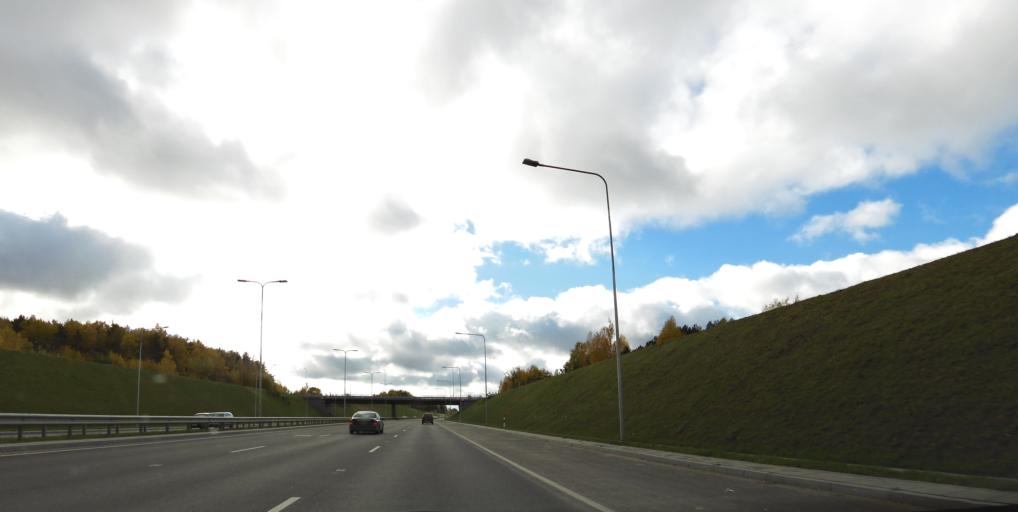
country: LT
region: Vilnius County
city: Pilaite
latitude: 54.6966
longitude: 25.2057
